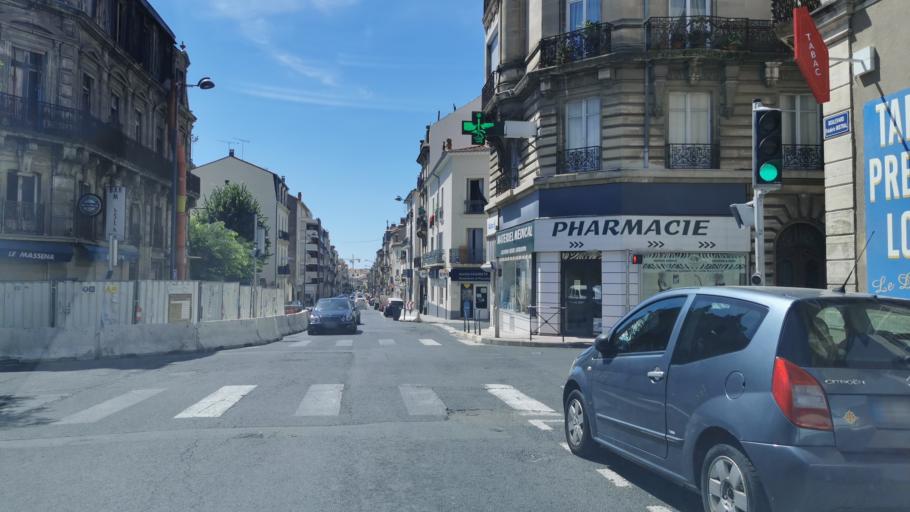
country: FR
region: Languedoc-Roussillon
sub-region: Departement de l'Herault
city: Beziers
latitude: 43.3450
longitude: 3.2199
